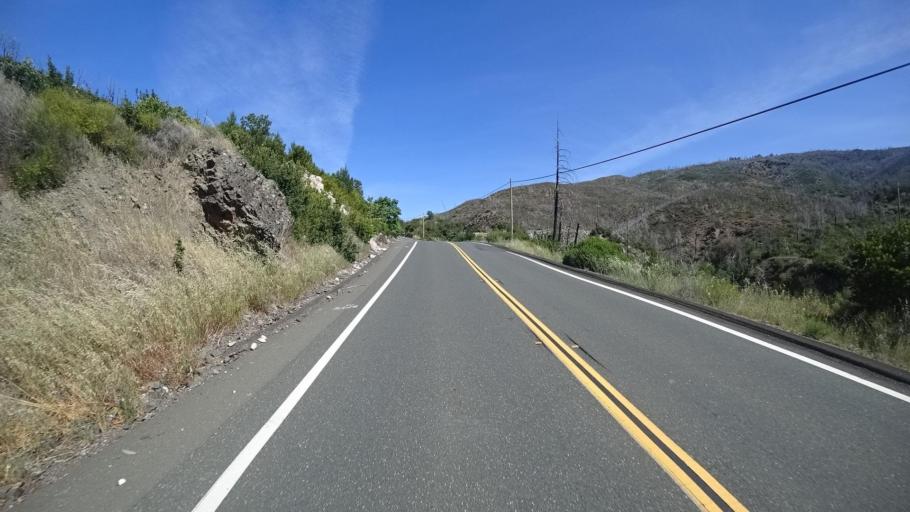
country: US
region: California
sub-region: Lake County
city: Cobb
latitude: 38.7904
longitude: -122.6950
